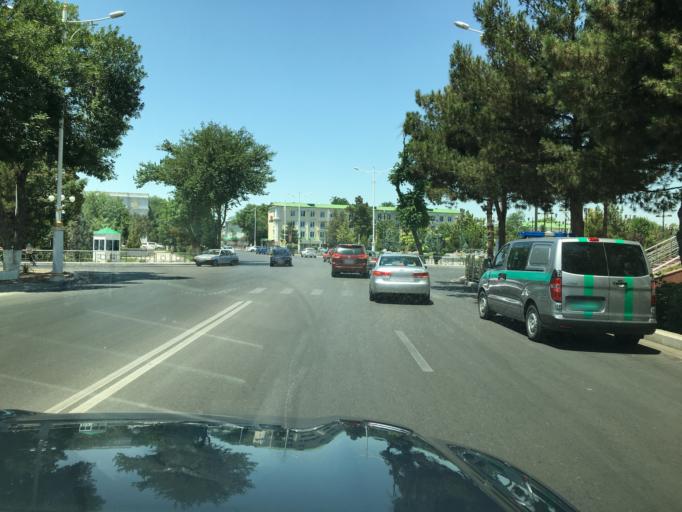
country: TM
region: Ahal
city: Ashgabat
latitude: 37.9409
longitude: 58.3778
